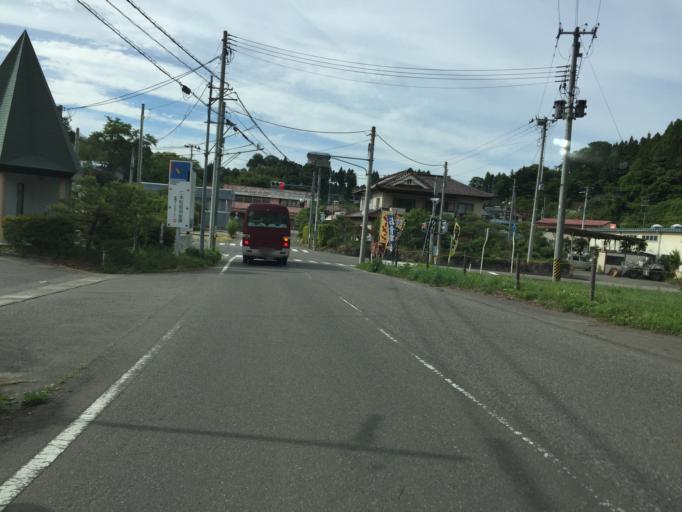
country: JP
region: Fukushima
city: Funehikimachi-funehiki
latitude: 37.5347
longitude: 140.5584
